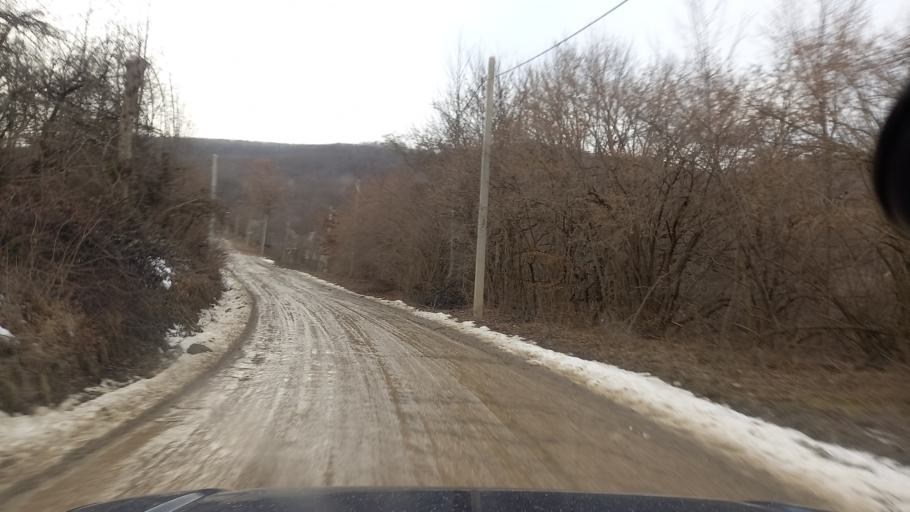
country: RU
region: Adygeya
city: Kamennomostskiy
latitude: 44.1415
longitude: 40.2798
